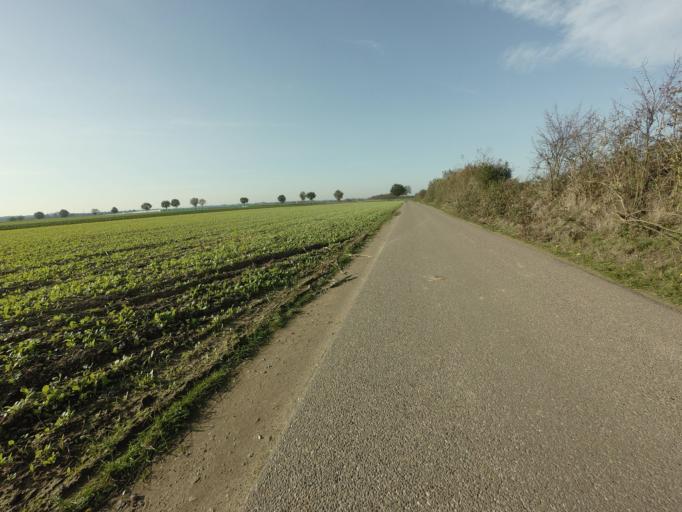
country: DE
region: North Rhine-Westphalia
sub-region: Regierungsbezirk Koln
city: Selfkant
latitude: 51.0440
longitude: 5.9253
